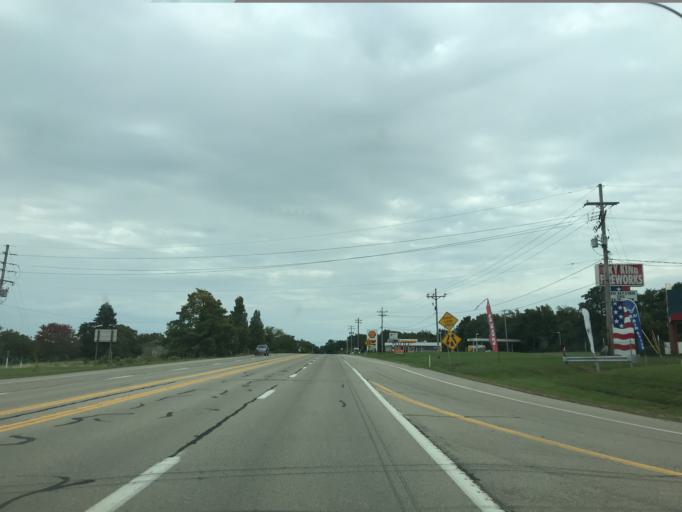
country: US
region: Pennsylvania
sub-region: Erie County
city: North East
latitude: 42.2344
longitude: -79.7778
